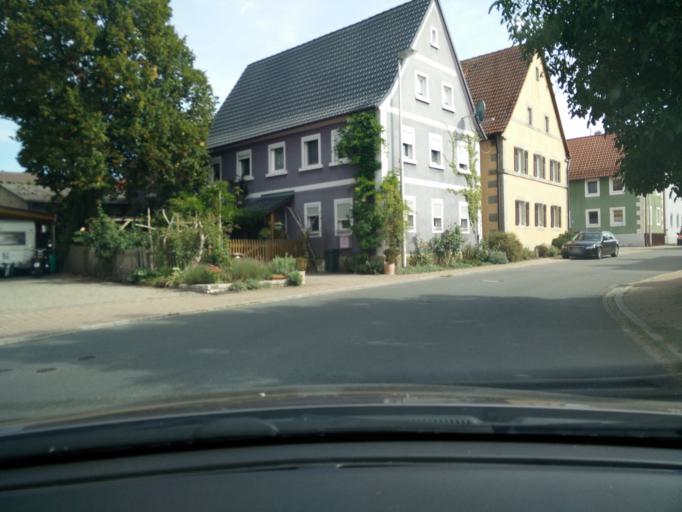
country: DE
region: Bavaria
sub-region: Regierungsbezirk Mittelfranken
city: Emskirchen
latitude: 49.5728
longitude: 10.7099
